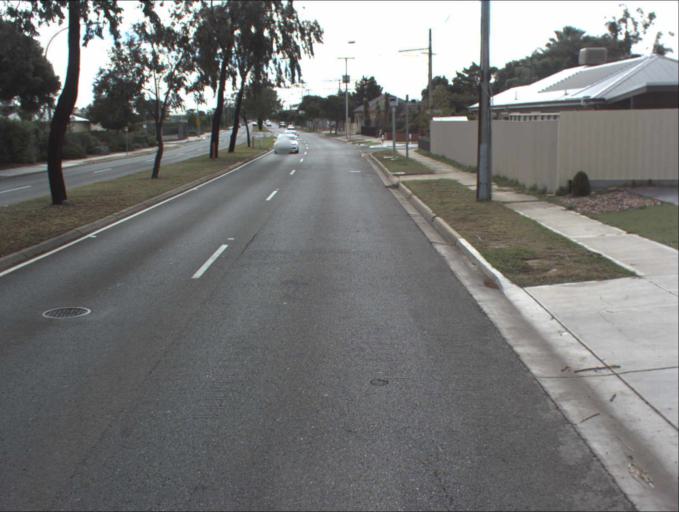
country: AU
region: South Australia
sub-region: Charles Sturt
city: Royal Park
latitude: -34.8732
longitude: 138.5036
